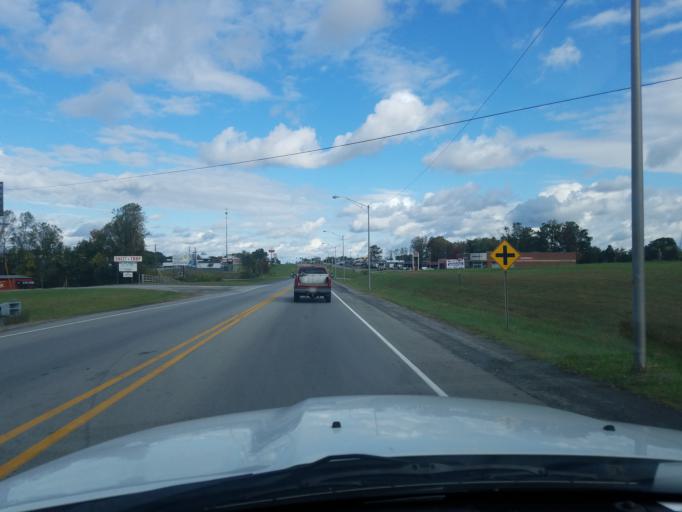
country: US
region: Kentucky
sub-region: Russell County
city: Russell Springs
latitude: 37.0575
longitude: -85.0707
